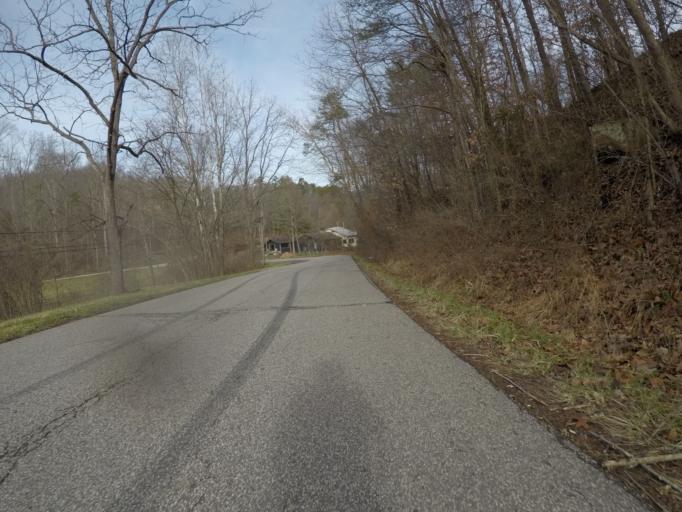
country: US
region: West Virginia
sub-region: Wayne County
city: Lavalette
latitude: 38.3523
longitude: -82.3737
